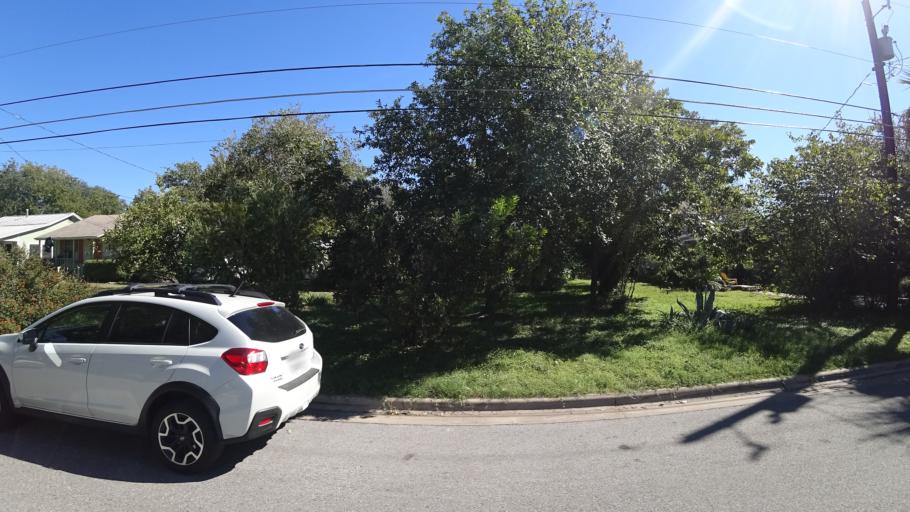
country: US
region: Texas
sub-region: Travis County
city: Austin
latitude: 30.3293
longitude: -97.7414
